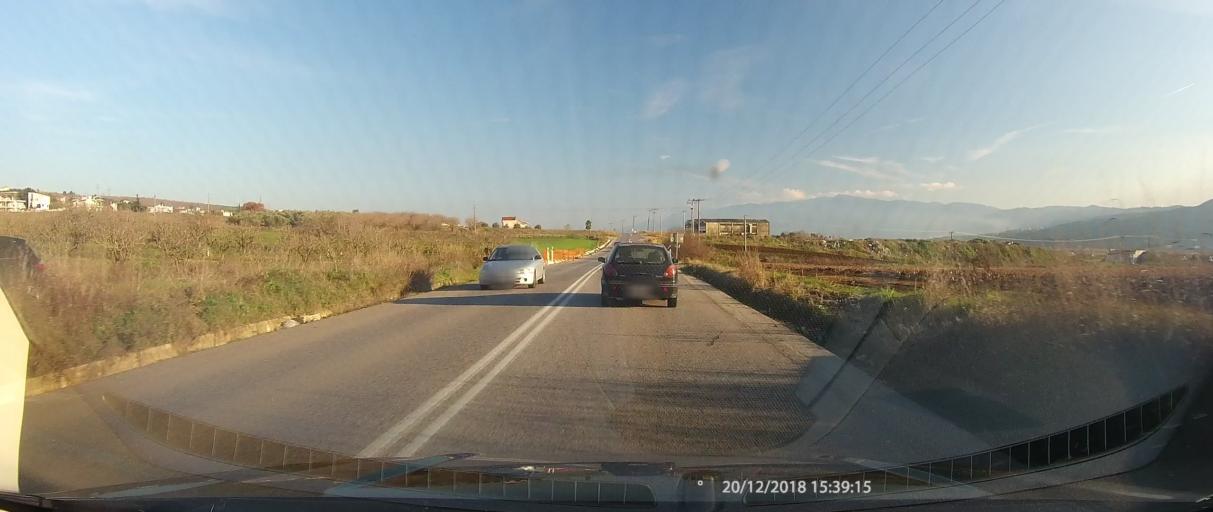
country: GR
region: Central Greece
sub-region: Nomos Fthiotidos
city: Stavros
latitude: 38.8978
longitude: 22.3616
